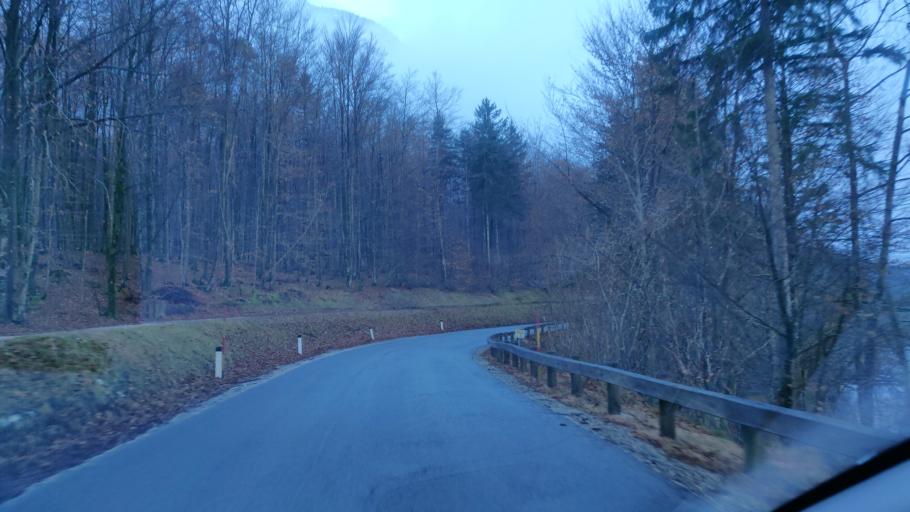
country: SI
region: Bohinj
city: Bohinjska Bistrica
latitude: 46.2806
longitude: 13.8460
